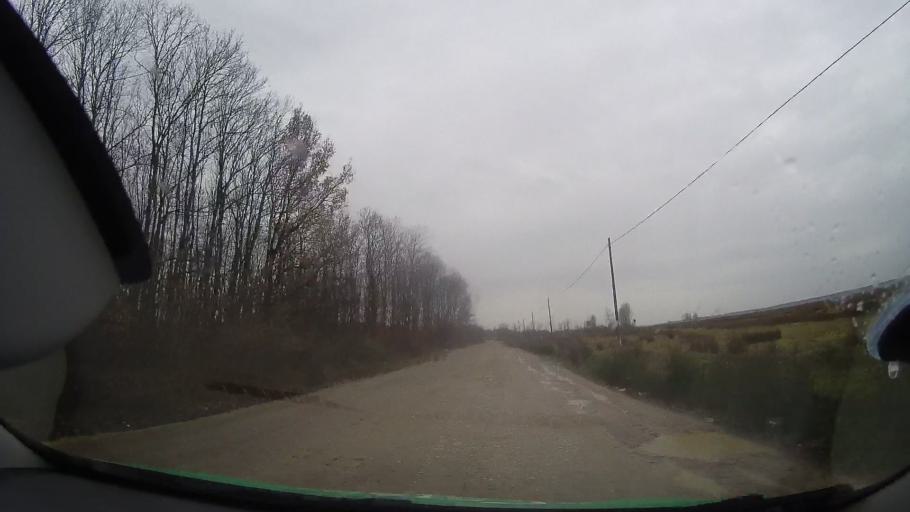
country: RO
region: Bihor
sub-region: Comuna Olcea
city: Olcea
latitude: 46.6886
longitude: 22.0044
